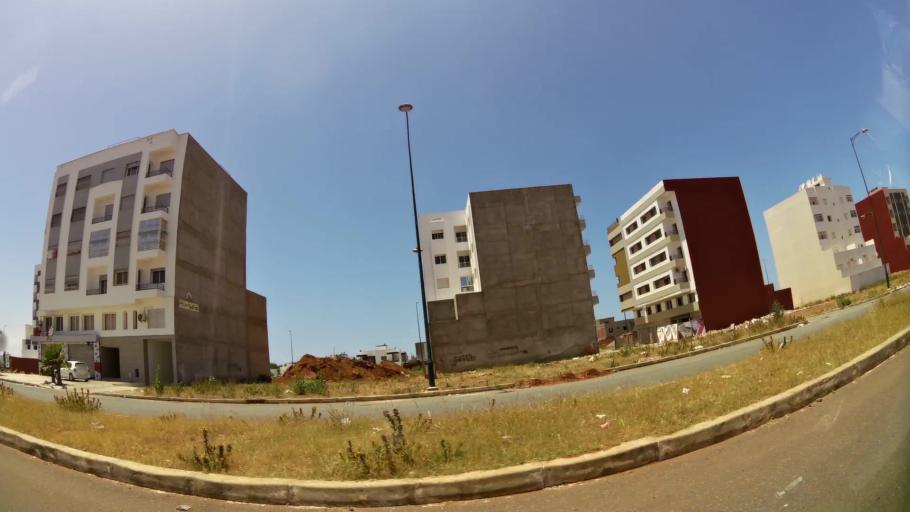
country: MA
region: Gharb-Chrarda-Beni Hssen
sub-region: Kenitra Province
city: Kenitra
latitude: 34.2689
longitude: -6.6274
